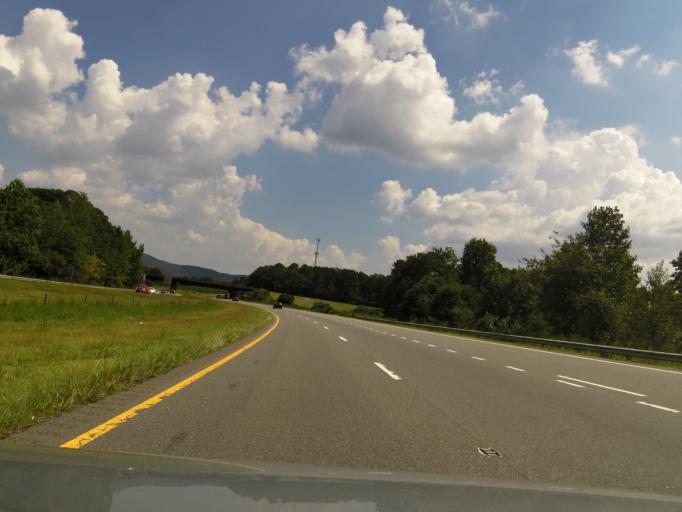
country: US
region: North Carolina
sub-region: Cleveland County
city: Kings Mountain
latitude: 35.2438
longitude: -81.3253
